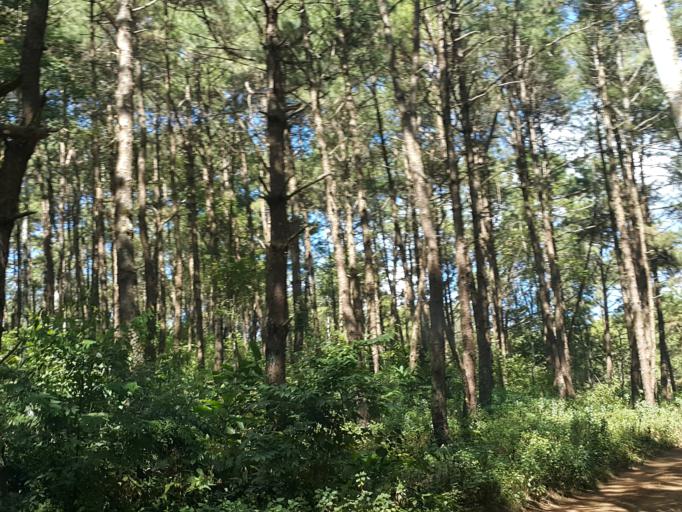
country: TH
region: Chiang Mai
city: Wiang Haeng
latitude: 19.5435
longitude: 98.8154
